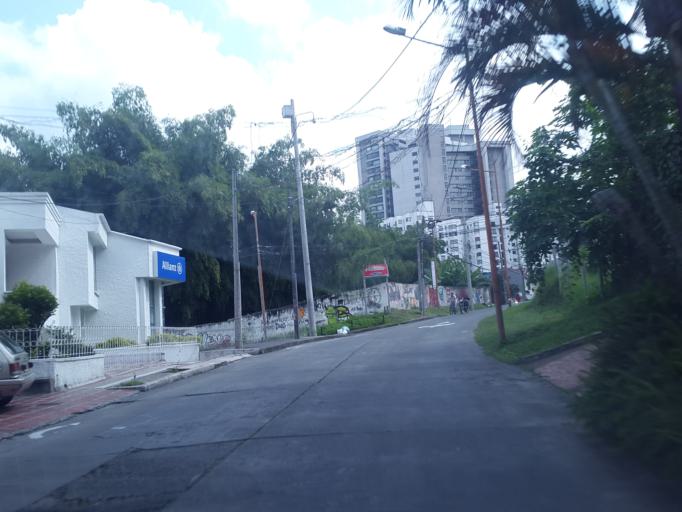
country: CO
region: Quindio
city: Armenia
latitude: 4.5488
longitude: -75.6621
